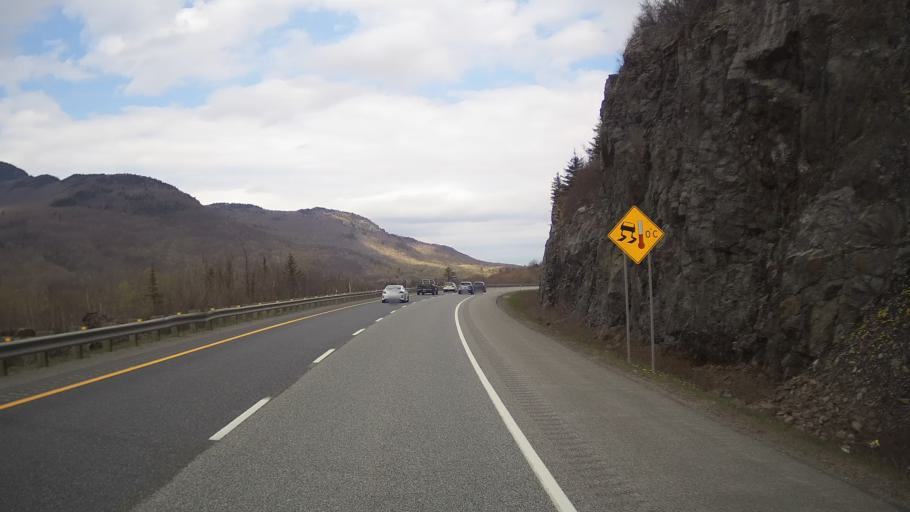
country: CA
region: Quebec
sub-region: Estrie
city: Magog
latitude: 45.2893
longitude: -72.2669
